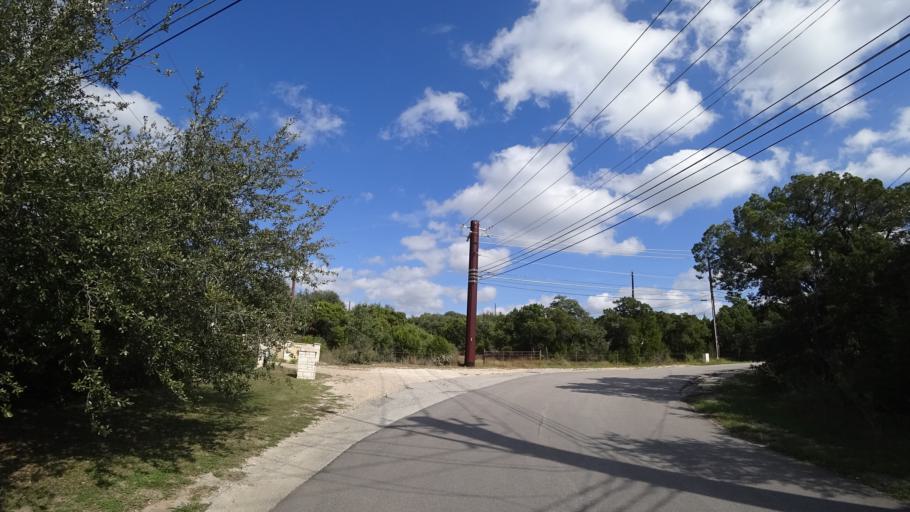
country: US
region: Texas
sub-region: Travis County
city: Barton Creek
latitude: 30.2580
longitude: -97.8870
